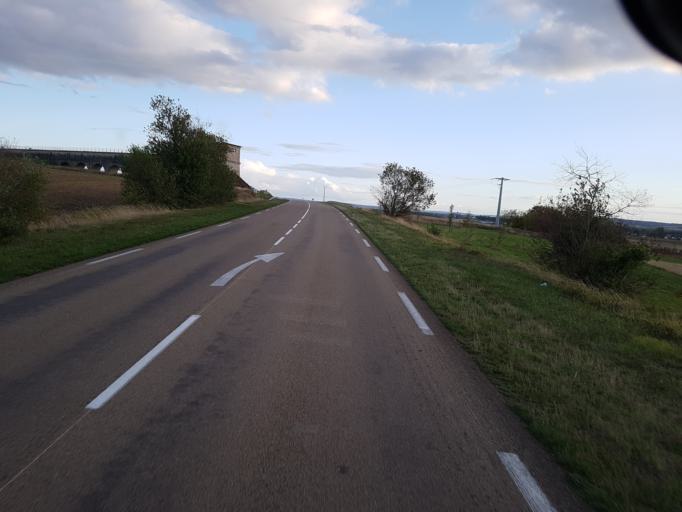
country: FR
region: Bourgogne
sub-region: Departement de l'Yonne
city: Soucy
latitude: 48.2738
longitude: 3.2728
